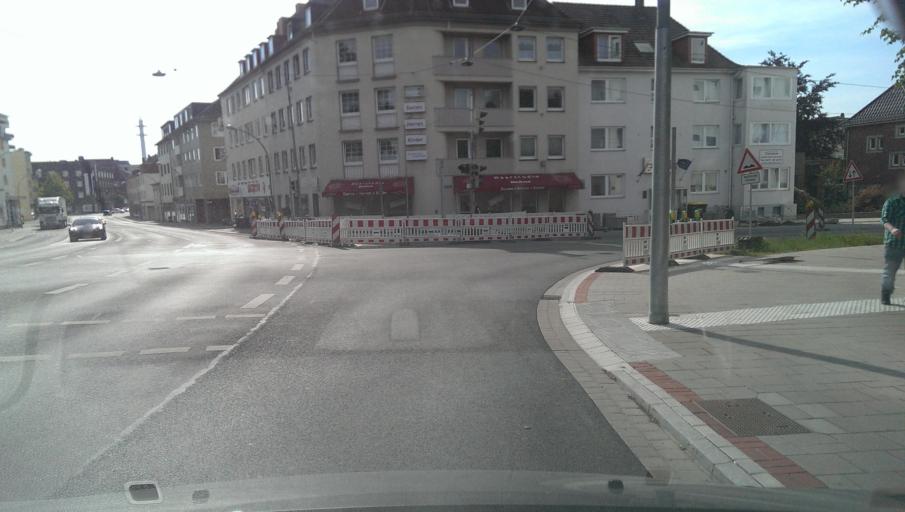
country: DE
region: Bremen
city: Bremerhaven
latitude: 53.5399
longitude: 8.5870
